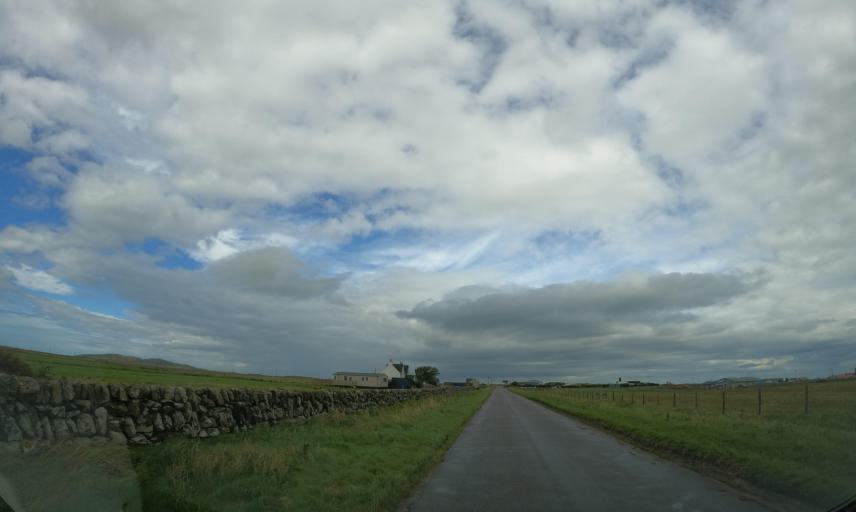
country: GB
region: Scotland
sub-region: Eilean Siar
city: Barra
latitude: 56.4936
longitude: -6.8834
